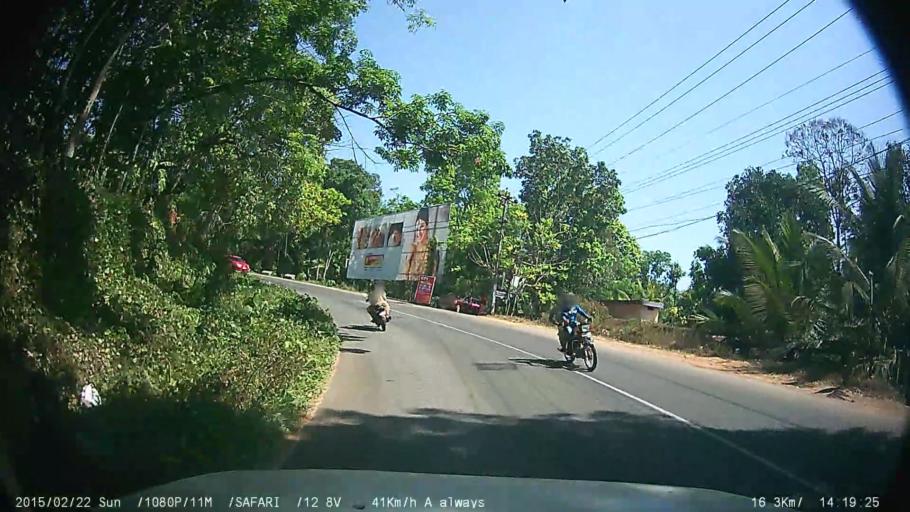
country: IN
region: Kerala
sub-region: Kottayam
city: Lalam
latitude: 9.5670
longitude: 76.6914
